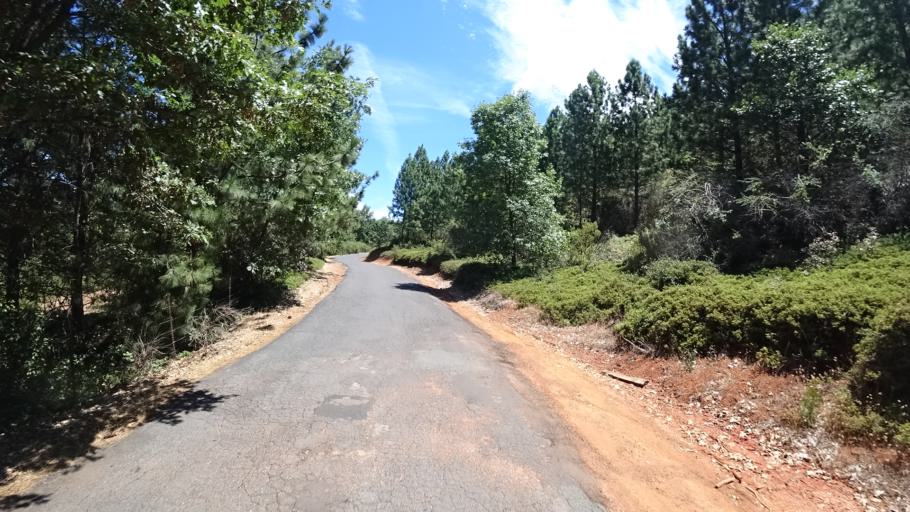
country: US
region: California
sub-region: Calaveras County
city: Forest Meadows
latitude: 38.1978
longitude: -120.4248
